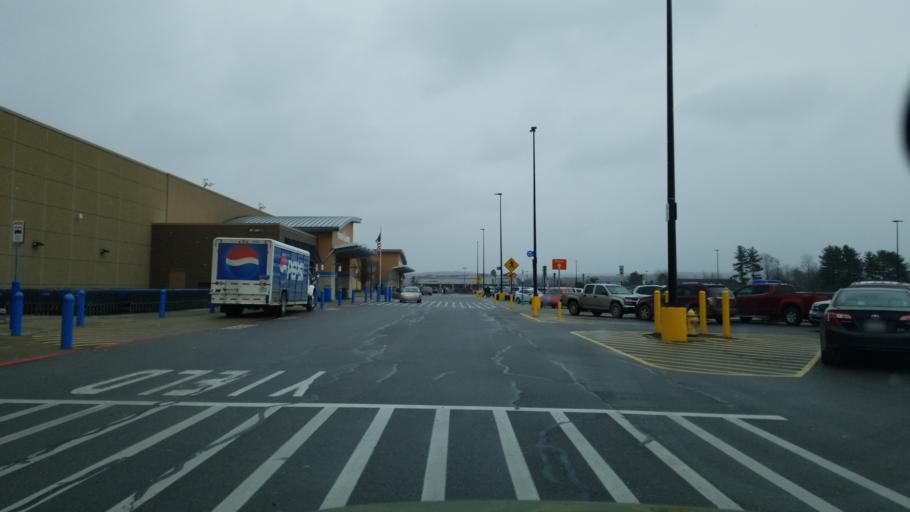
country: US
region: Pennsylvania
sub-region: Clearfield County
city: DuBois
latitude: 41.1278
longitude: -78.7387
